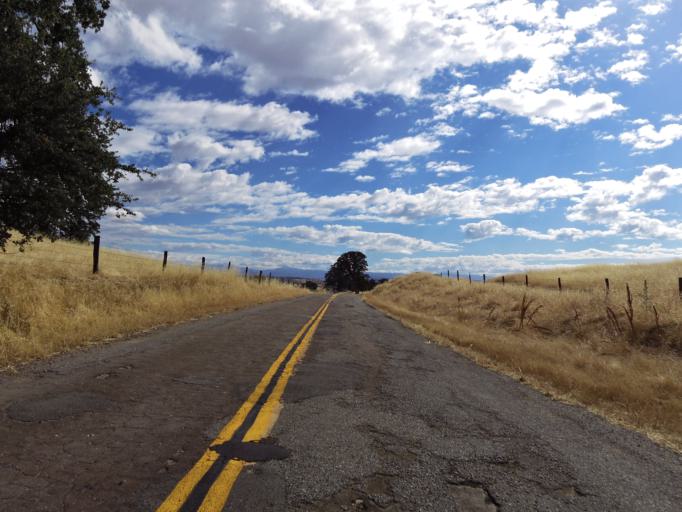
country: US
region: California
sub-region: Madera County
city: Bonadelle Ranchos-Madera Ranchos
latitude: 37.0451
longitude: -119.7567
